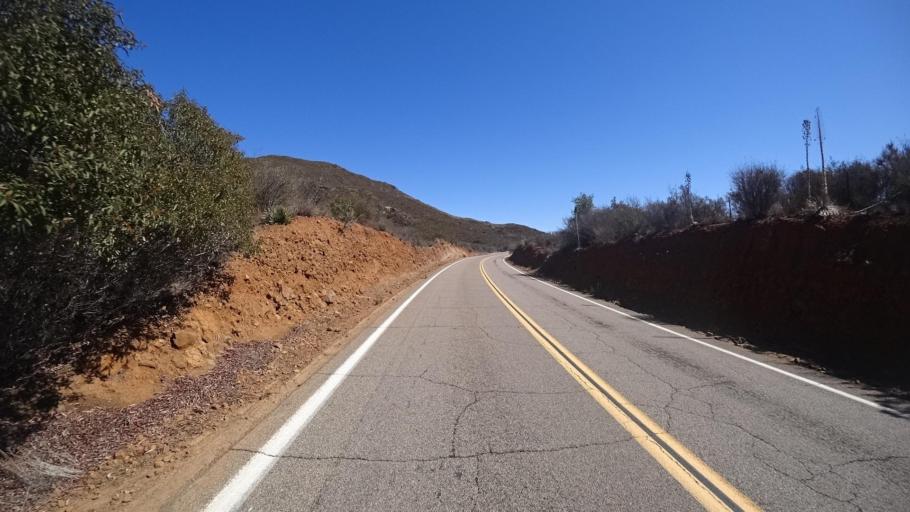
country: US
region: California
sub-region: San Diego County
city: Alpine
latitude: 32.7082
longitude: -116.7140
